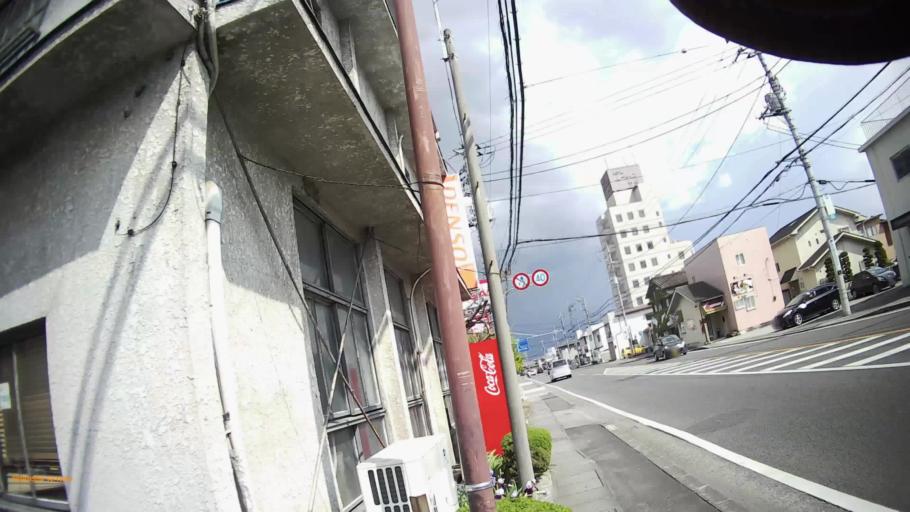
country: JP
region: Yamanashi
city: Kofu-shi
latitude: 35.6594
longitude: 138.5453
